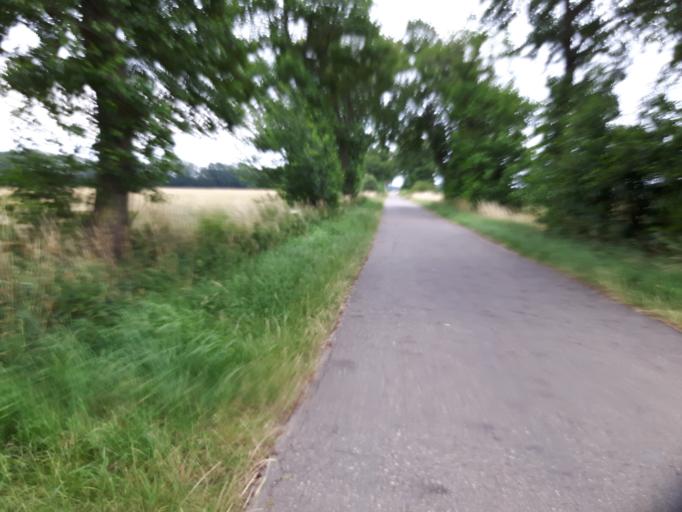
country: DE
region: Lower Saxony
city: Winsen
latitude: 53.3803
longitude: 10.1663
